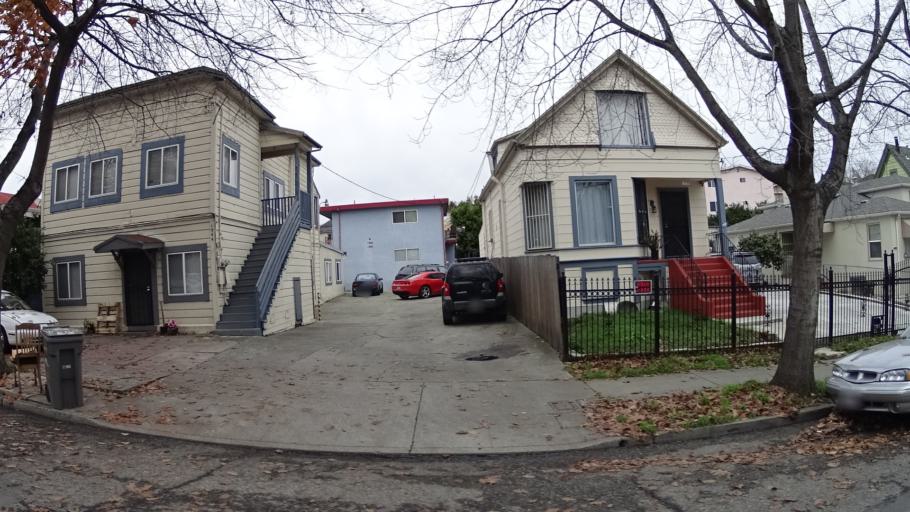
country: US
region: California
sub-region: Alameda County
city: Alameda
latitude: 37.7932
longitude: -122.2331
